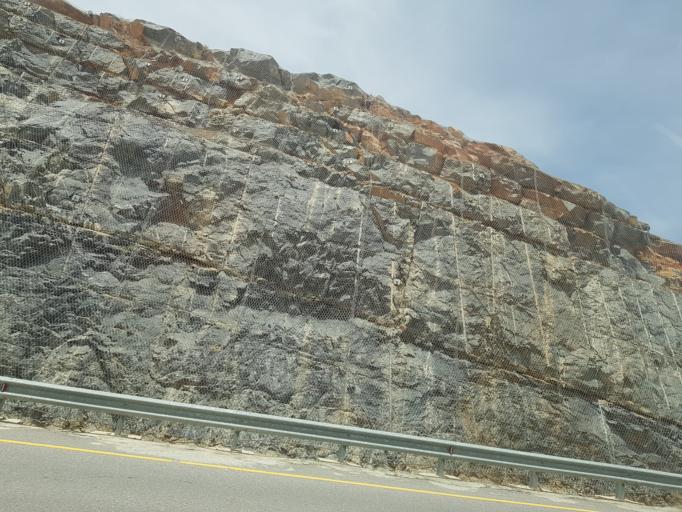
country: OM
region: Muhafazat ad Dakhiliyah
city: Izki
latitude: 23.0021
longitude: 57.7008
